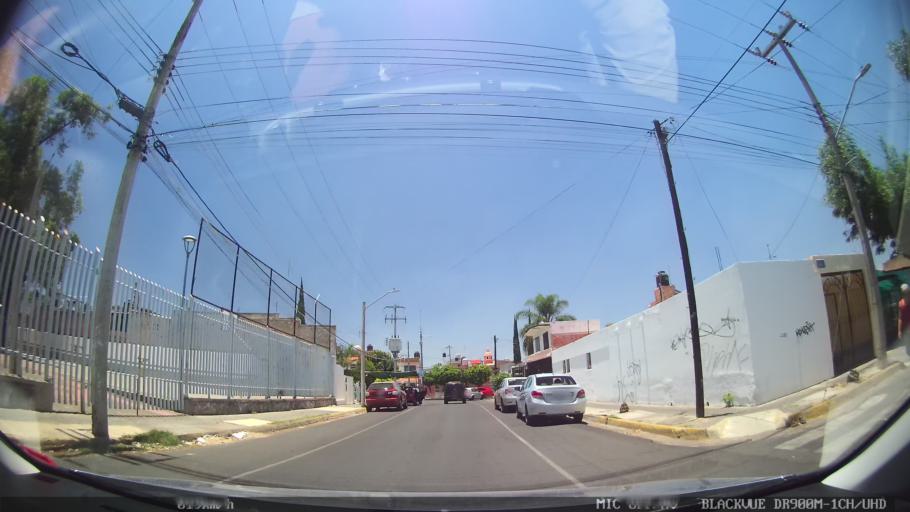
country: MX
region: Jalisco
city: Tlaquepaque
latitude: 20.6775
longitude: -103.2841
